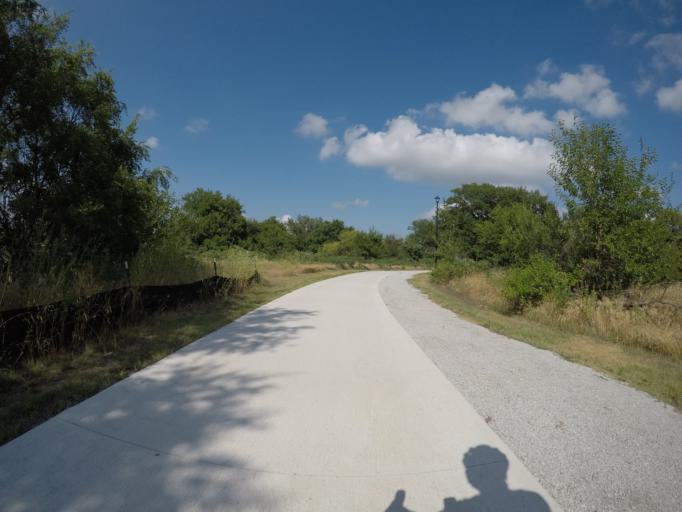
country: US
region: Nebraska
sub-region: Buffalo County
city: Kearney
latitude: 40.6725
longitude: -99.0316
